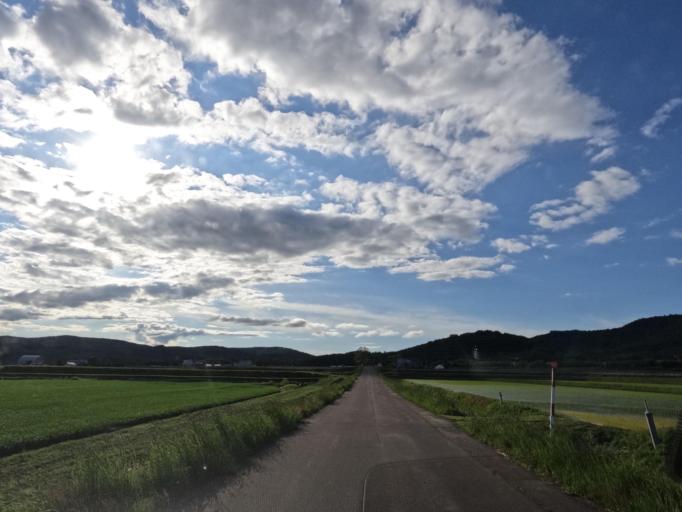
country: JP
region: Hokkaido
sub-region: Asahikawa-shi
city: Asahikawa
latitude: 43.9169
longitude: 142.4963
